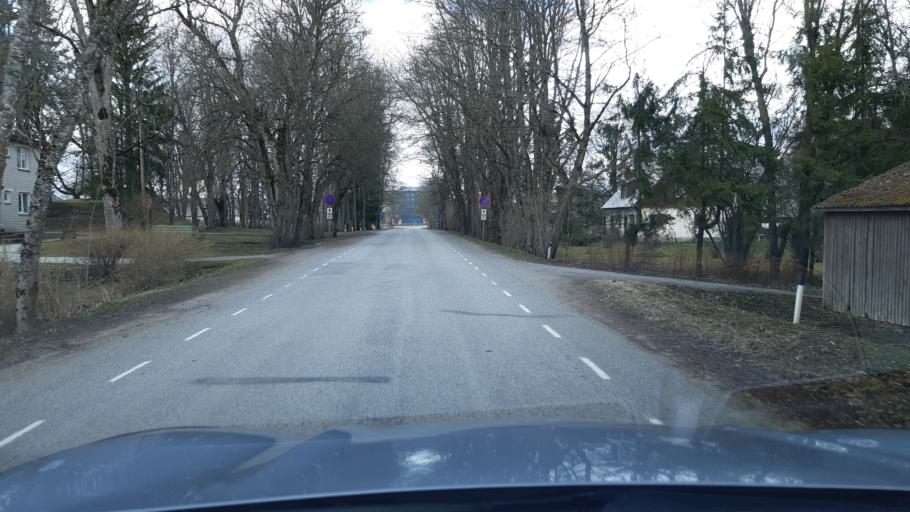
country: EE
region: Raplamaa
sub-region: Kehtna vald
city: Kehtna
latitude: 59.0434
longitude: 25.1185
